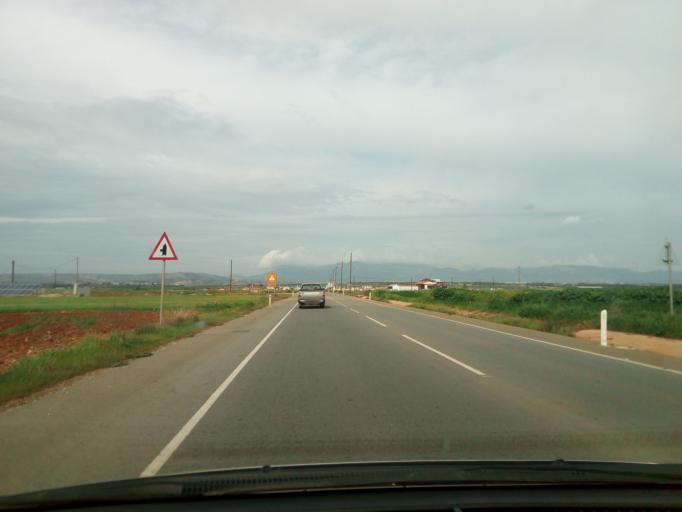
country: CY
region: Lefkosia
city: Akaki
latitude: 35.1438
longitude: 33.1559
